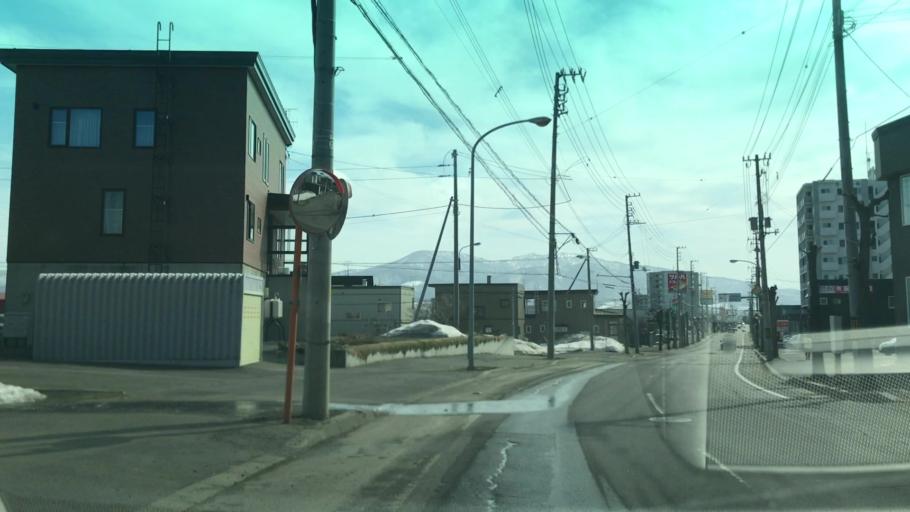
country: JP
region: Hokkaido
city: Yoichi
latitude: 43.1907
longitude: 140.7999
